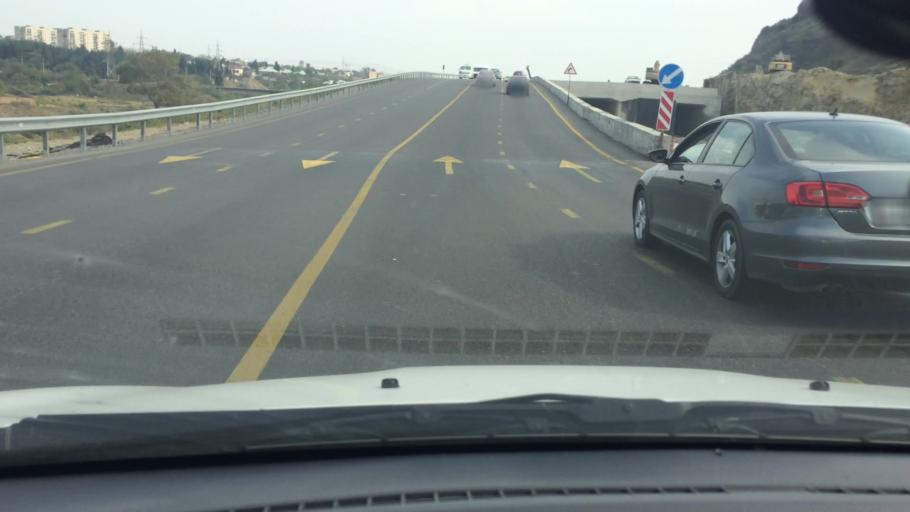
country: GE
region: T'bilisi
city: Tbilisi
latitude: 41.6620
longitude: 44.8830
